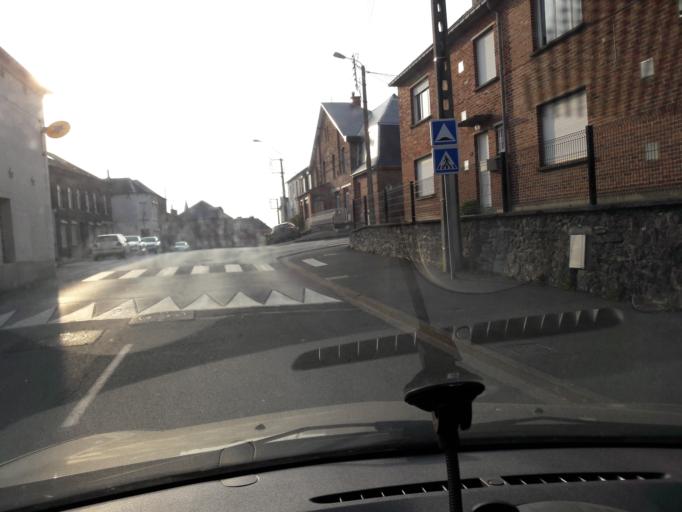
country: FR
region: Nord-Pas-de-Calais
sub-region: Departement du Nord
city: Boussois
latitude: 50.2888
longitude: 4.0458
